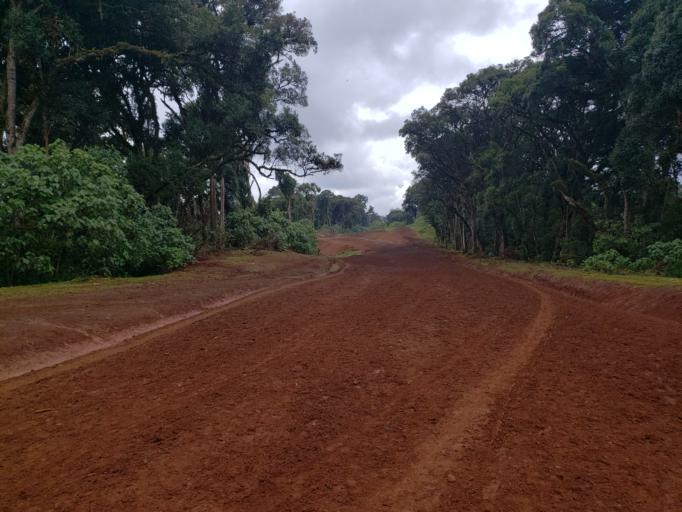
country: ET
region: Oromiya
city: Dodola
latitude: 6.6130
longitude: 39.4183
